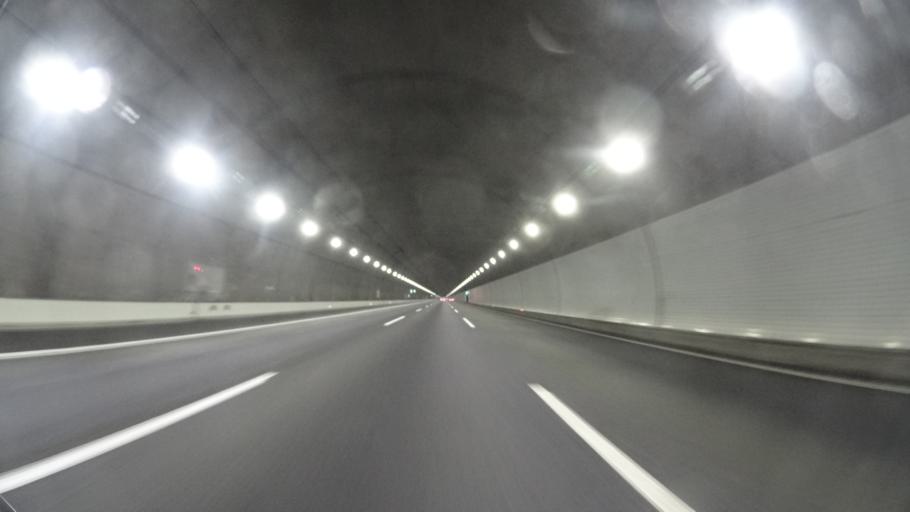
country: JP
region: Shizuoka
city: Fujinomiya
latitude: 35.1615
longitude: 138.5696
